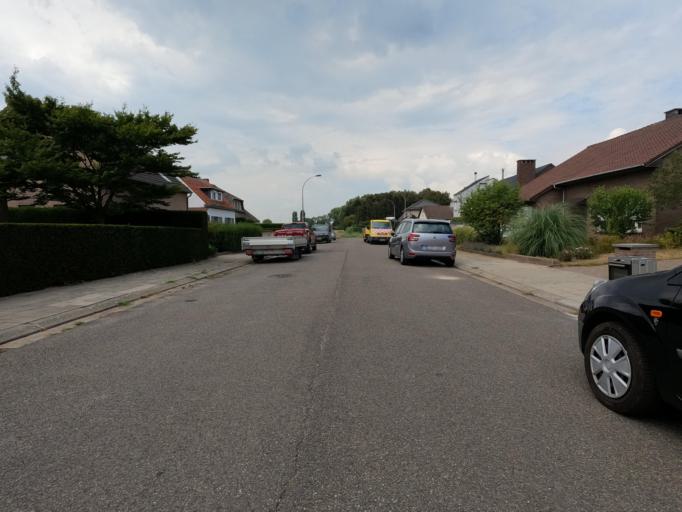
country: BE
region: Flanders
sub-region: Provincie Antwerpen
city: Stabroek
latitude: 51.3095
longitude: 4.3982
